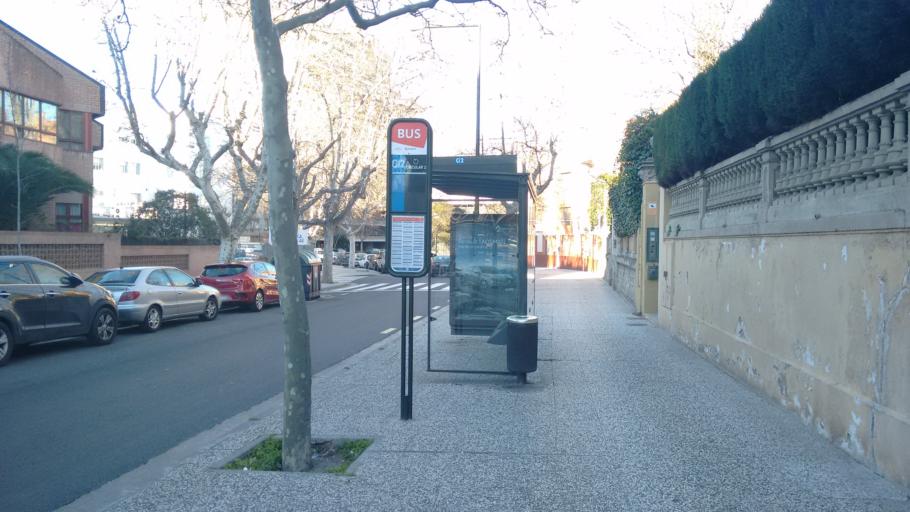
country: ES
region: Aragon
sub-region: Provincia de Zaragoza
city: Delicias
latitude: 41.6362
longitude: -0.8893
